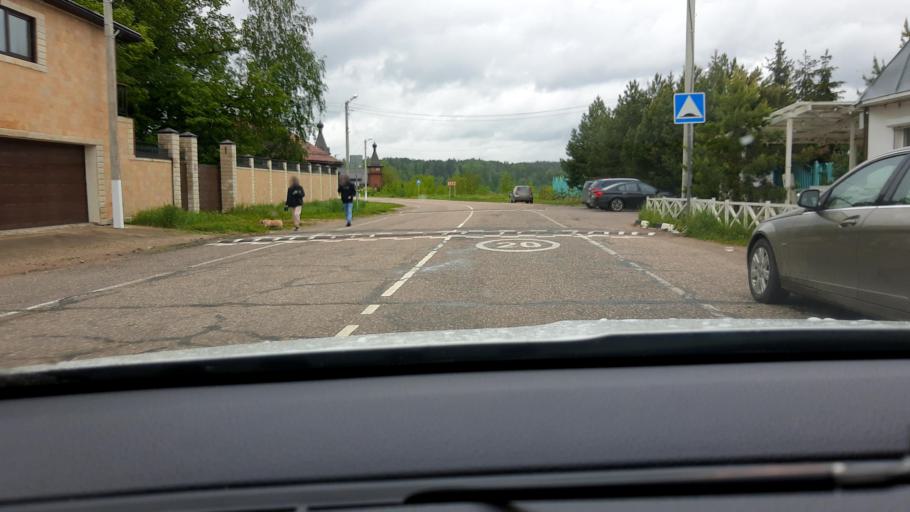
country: RU
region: Moskovskaya
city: Zvenigorod
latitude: 55.7327
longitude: 36.9209
